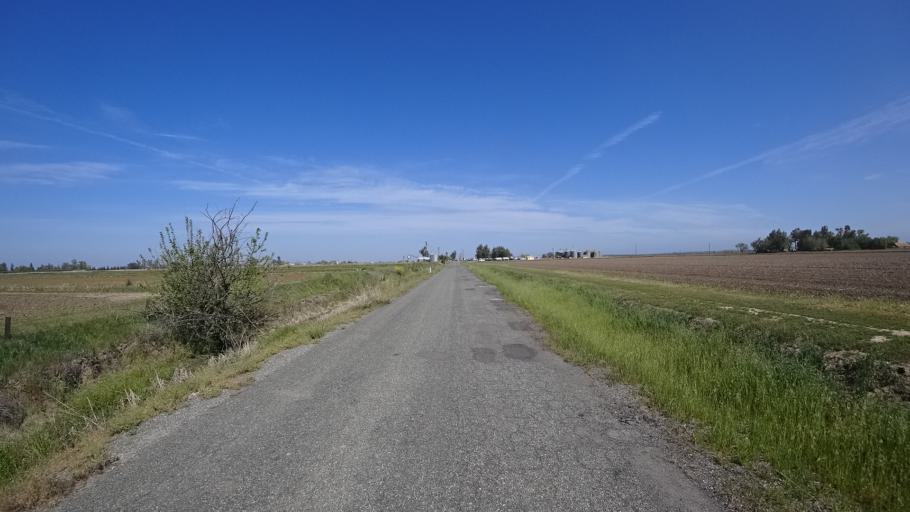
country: US
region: California
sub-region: Glenn County
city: Hamilton City
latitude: 39.5768
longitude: -122.0276
